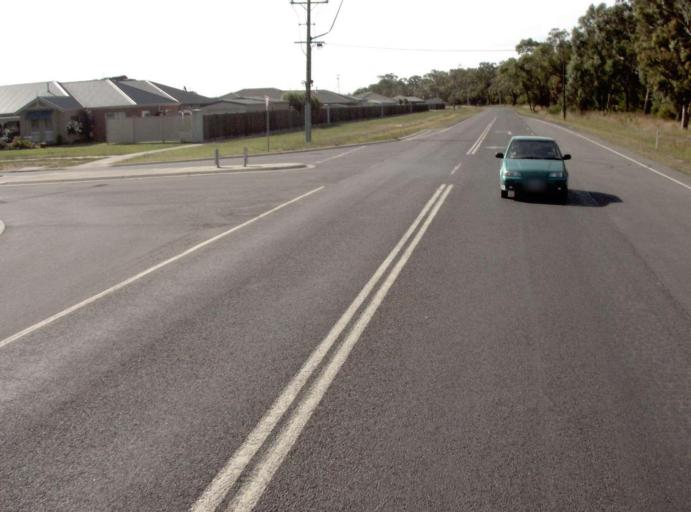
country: AU
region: Victoria
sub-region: Latrobe
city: Moe
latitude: -38.1681
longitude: 146.2794
